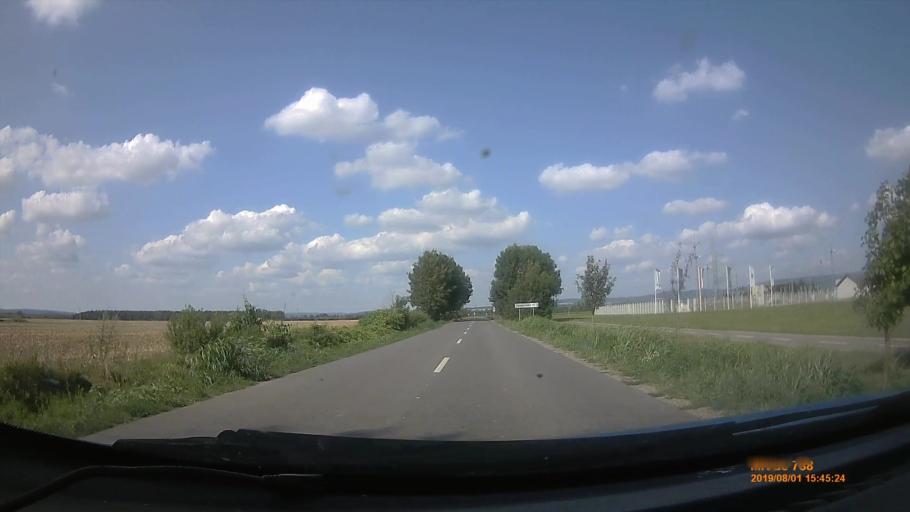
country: HU
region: Baranya
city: Szentlorinc
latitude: 46.0158
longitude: 17.9770
